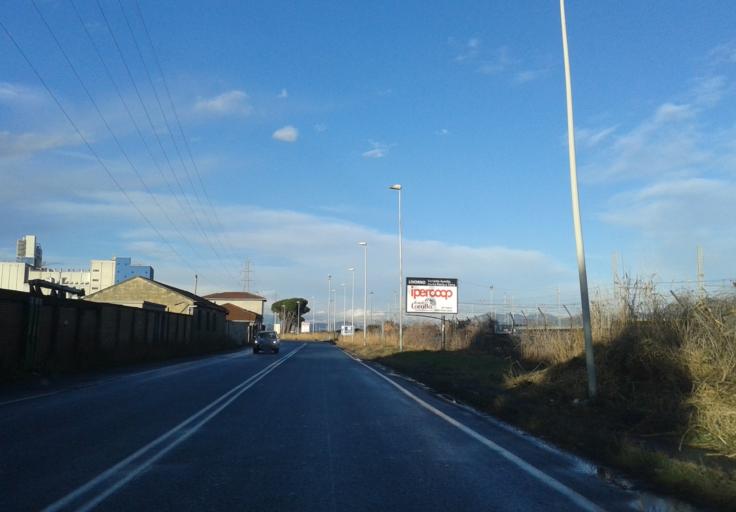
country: IT
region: Tuscany
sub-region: Provincia di Livorno
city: Livorno
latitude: 43.5750
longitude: 10.3206
